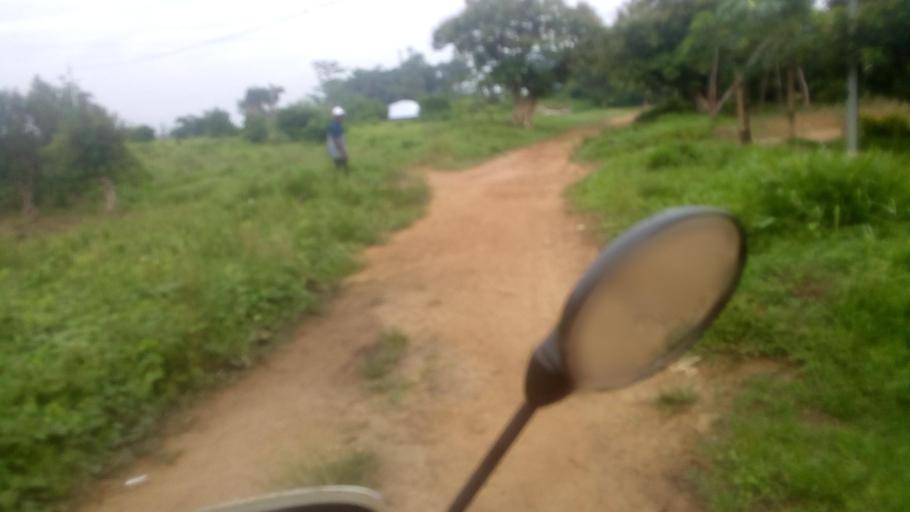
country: SL
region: Eastern Province
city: Pendembu
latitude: 8.0951
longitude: -10.6961
